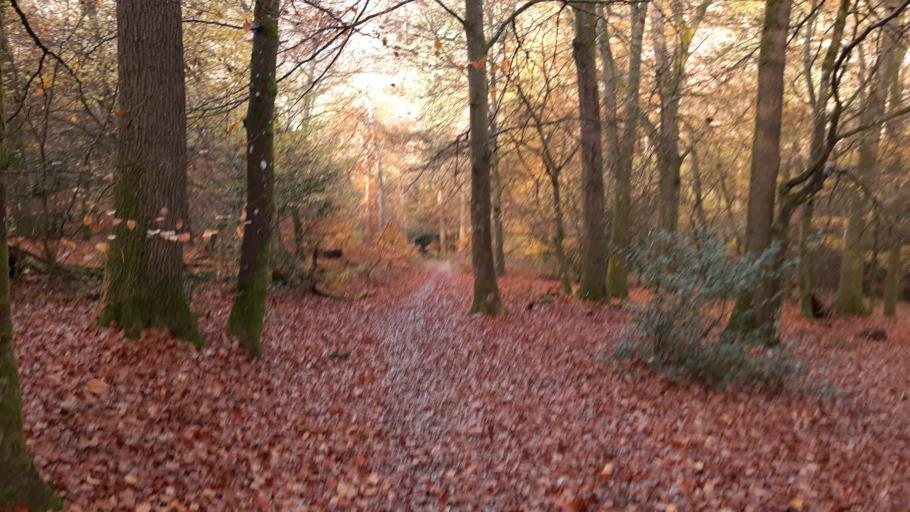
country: DE
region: Saarland
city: Orscholz
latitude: 49.4998
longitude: 6.5492
